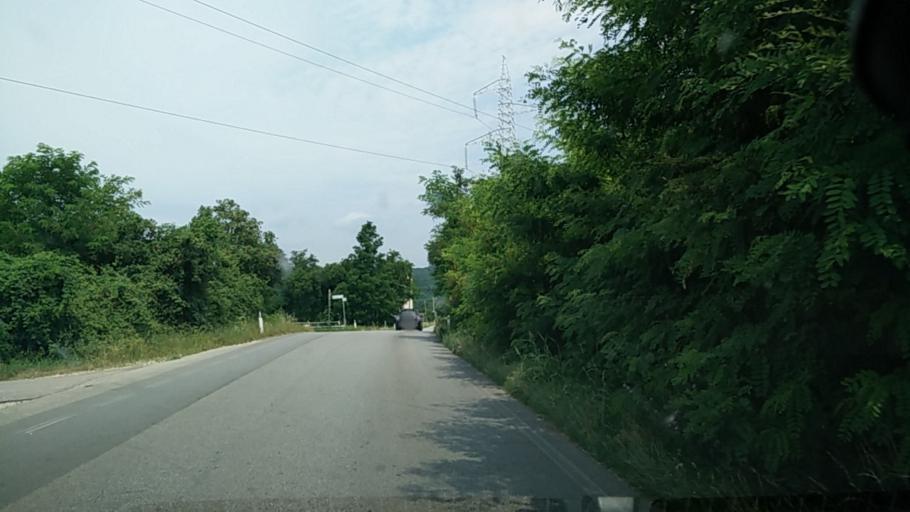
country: IT
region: Veneto
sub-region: Provincia di Treviso
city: Selva del Montello
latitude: 45.7763
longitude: 12.1392
